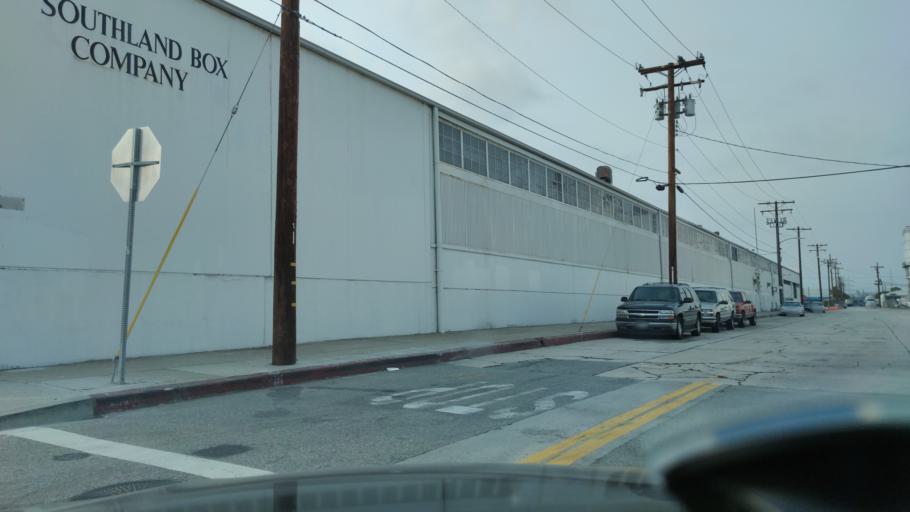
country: US
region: California
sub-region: Los Angeles County
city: Maywood
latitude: 33.9963
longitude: -118.2027
